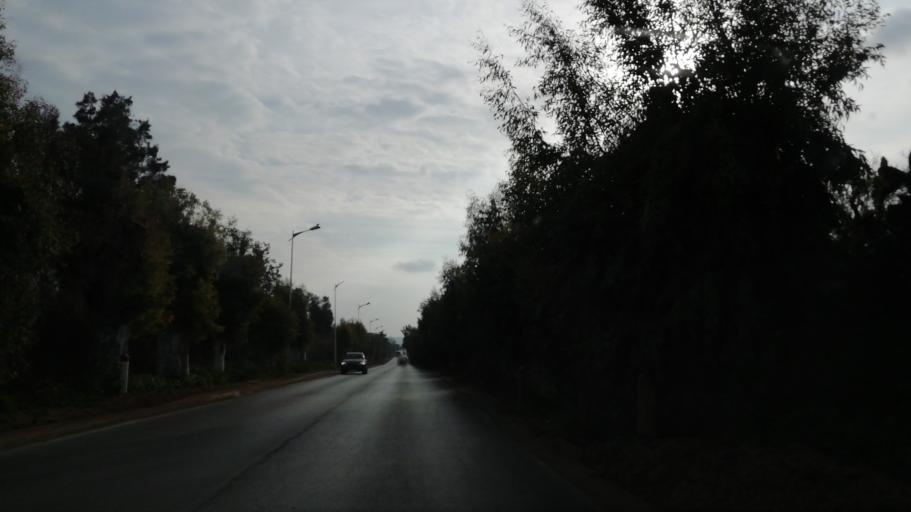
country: DZ
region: Mostaganem
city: Mostaganem
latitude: 35.8727
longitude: 0.0774
